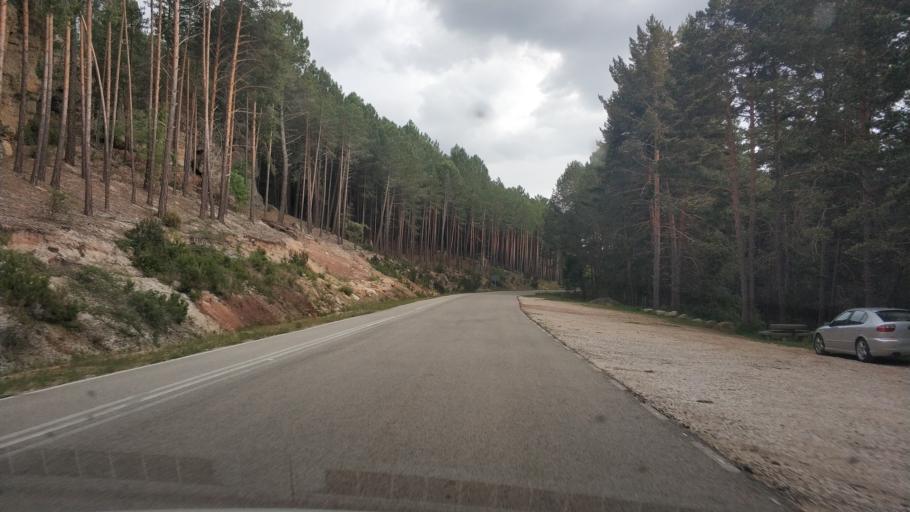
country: ES
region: Castille and Leon
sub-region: Provincia de Soria
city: San Leonardo de Yague
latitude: 41.8441
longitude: -3.0679
